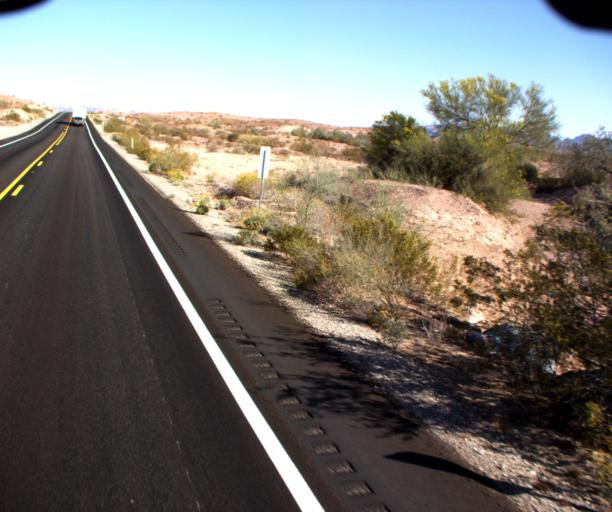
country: US
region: Arizona
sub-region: Yuma County
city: Wellton
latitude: 33.0719
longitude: -114.2943
